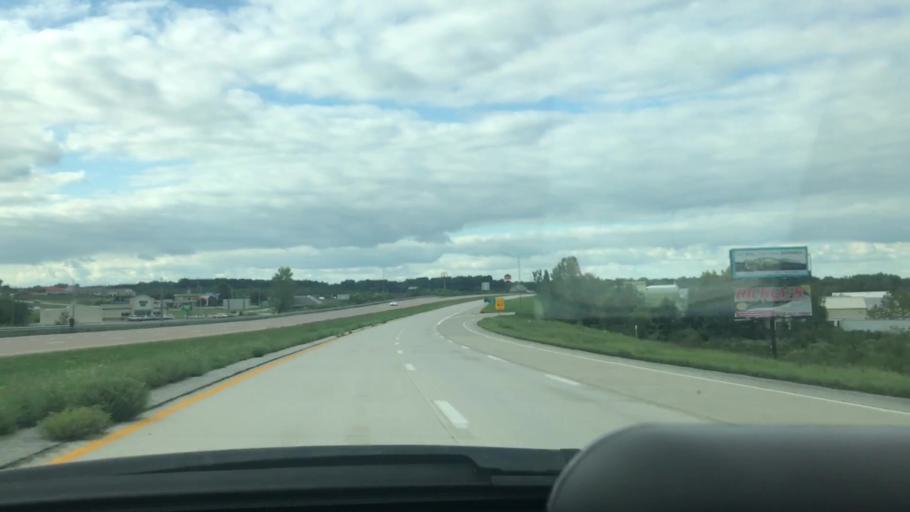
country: US
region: Missouri
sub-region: Benton County
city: Warsaw
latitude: 38.2618
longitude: -93.3661
